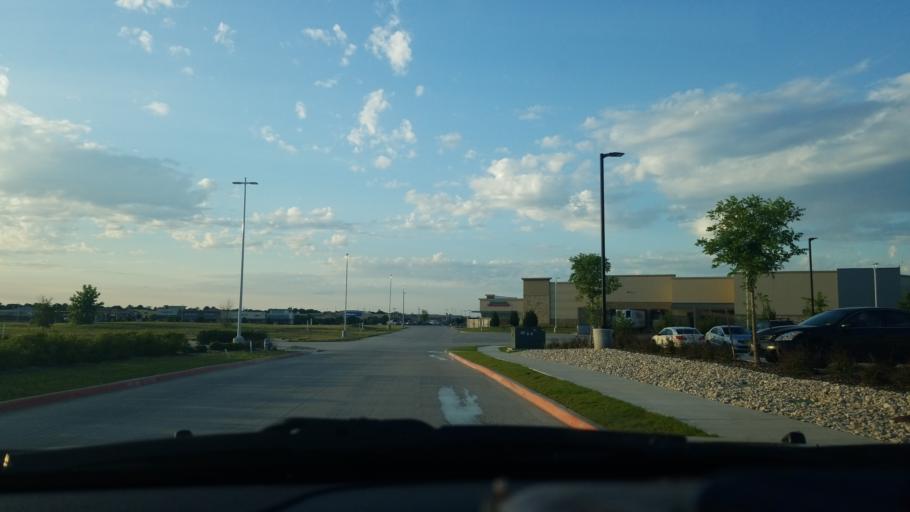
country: US
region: Texas
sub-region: Denton County
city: Denton
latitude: 33.2261
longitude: -97.1678
